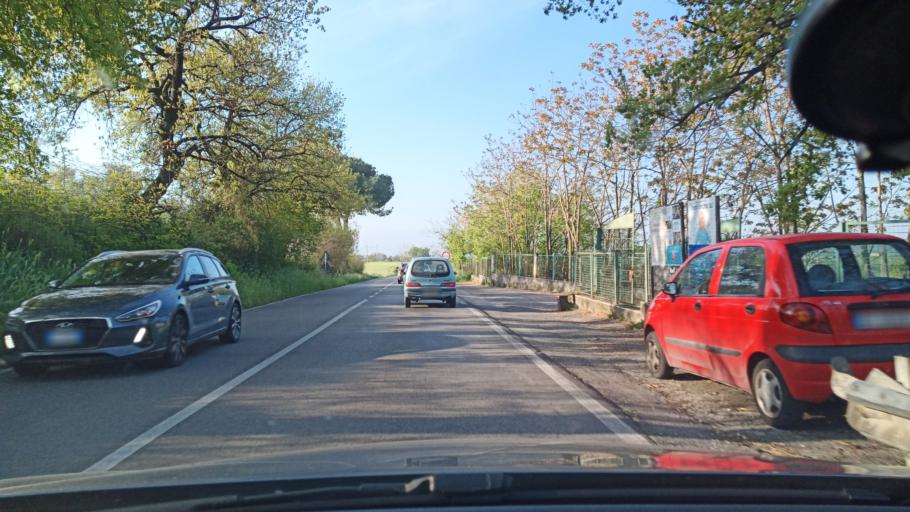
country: IT
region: Latium
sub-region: Citta metropolitana di Roma Capitale
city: Fiano Romano
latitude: 42.1831
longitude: 12.6365
